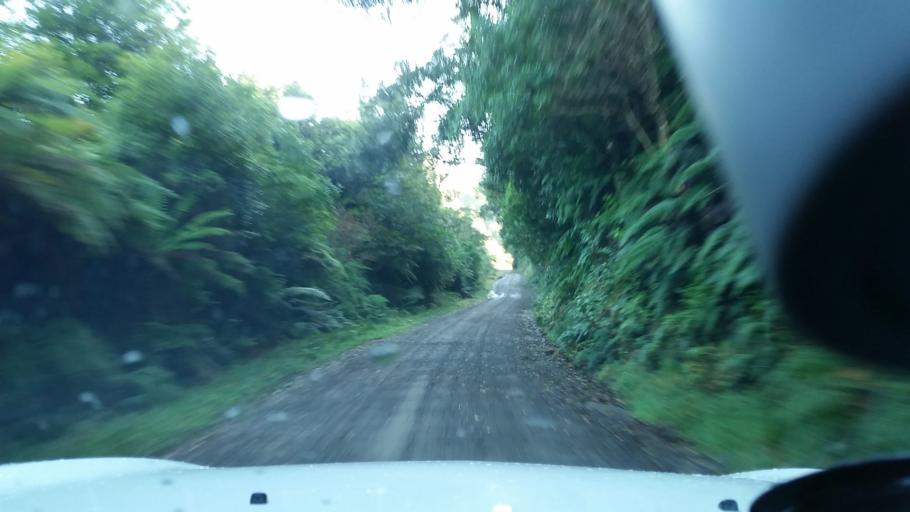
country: NZ
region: Bay of Plenty
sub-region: Kawerau District
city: Kawerau
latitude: -38.0055
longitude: 176.5979
